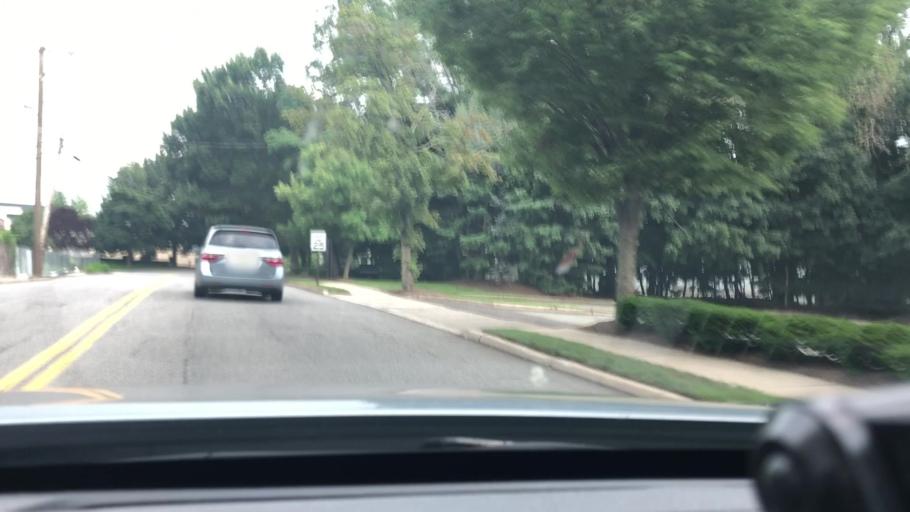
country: US
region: New Jersey
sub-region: Bergen County
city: Paramus
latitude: 40.9636
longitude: -74.0731
